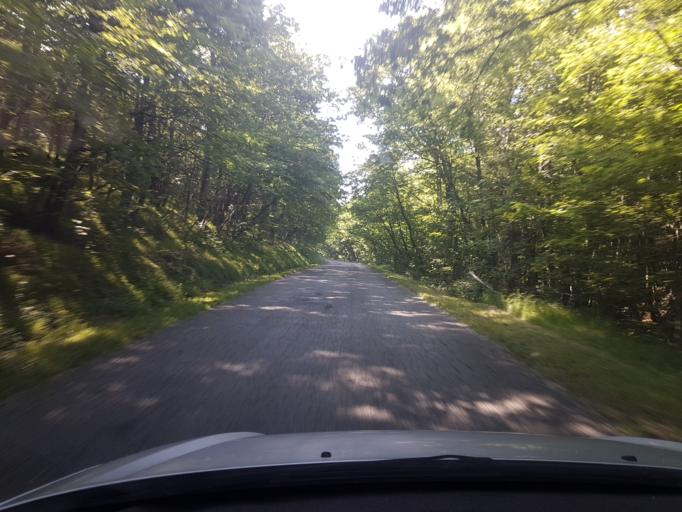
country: SI
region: Divaca
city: Divaca
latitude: 45.7573
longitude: 13.9923
